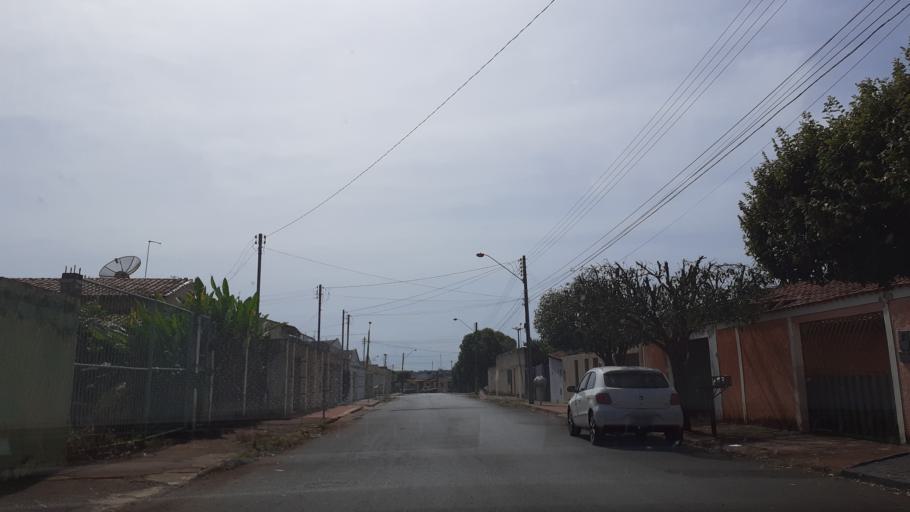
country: BR
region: Goias
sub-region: Itumbiara
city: Itumbiara
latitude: -18.4163
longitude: -49.2301
